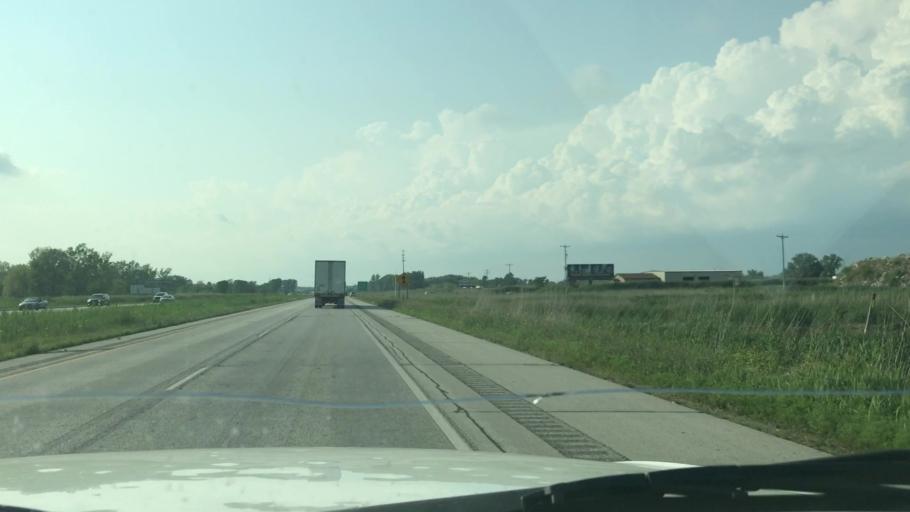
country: US
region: Wisconsin
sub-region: Brown County
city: Green Bay
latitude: 44.5421
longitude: -88.0283
